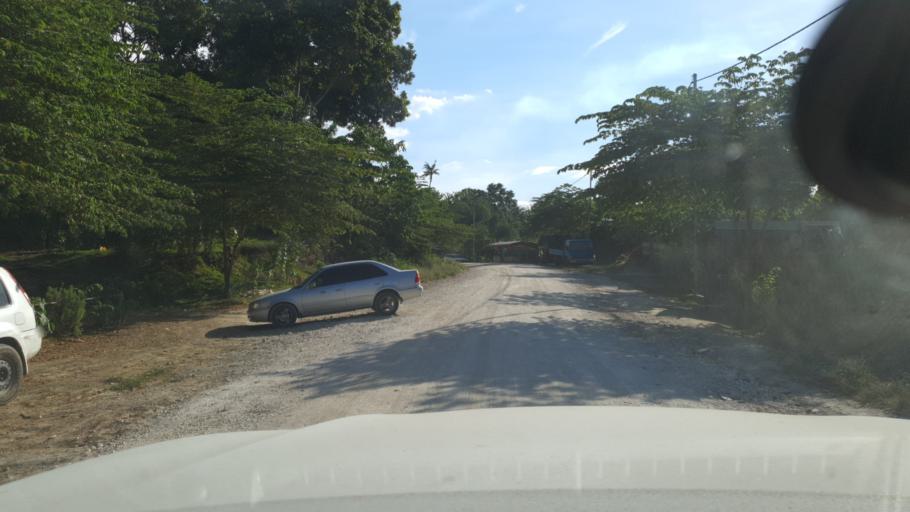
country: SB
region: Guadalcanal
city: Honiara
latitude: -9.4459
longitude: 159.9984
